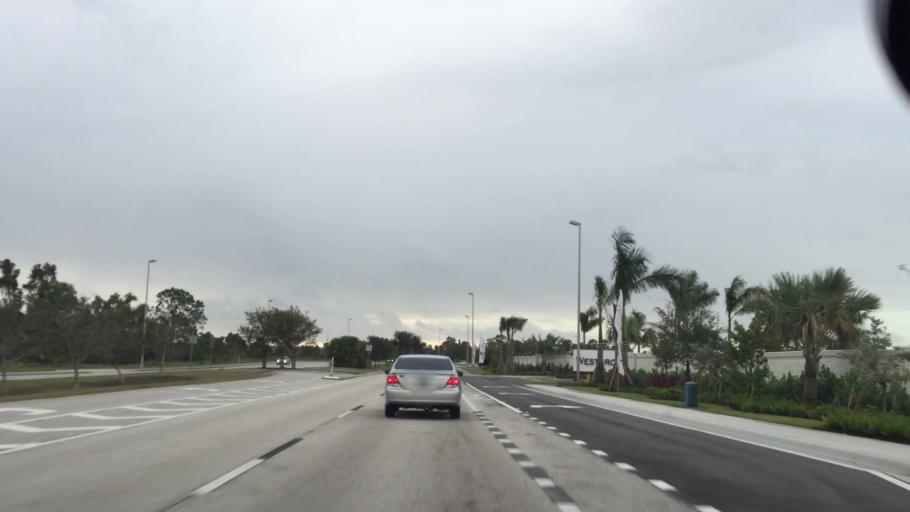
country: US
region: Florida
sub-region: Lee County
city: Three Oaks
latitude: 26.4899
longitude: -81.8005
